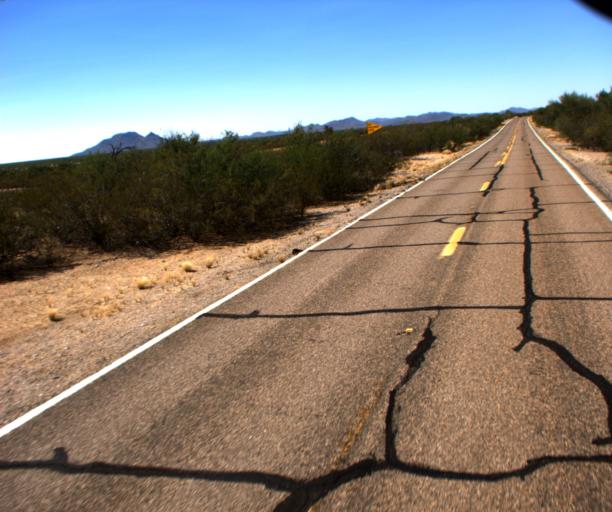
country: US
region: Arizona
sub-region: Pima County
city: Three Points
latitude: 31.9546
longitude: -111.3885
